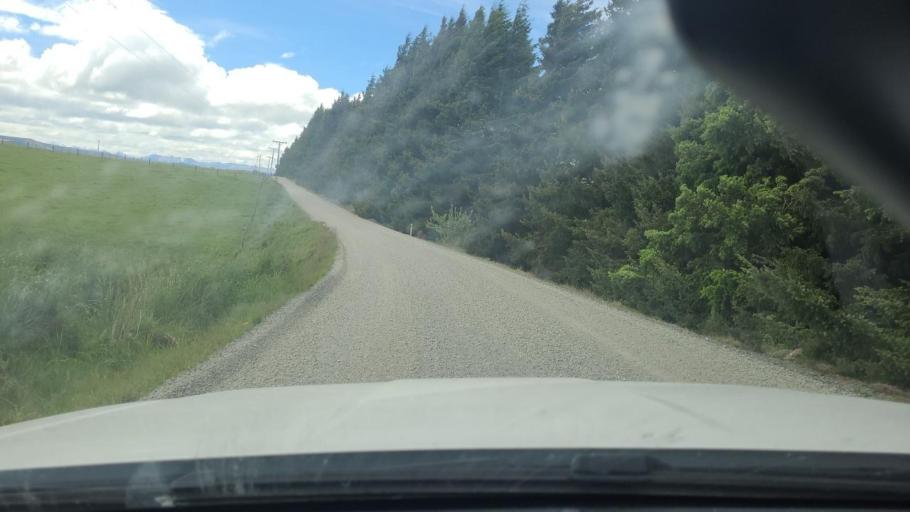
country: NZ
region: Southland
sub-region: Southland District
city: Te Anau
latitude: -45.4889
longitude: 167.8179
